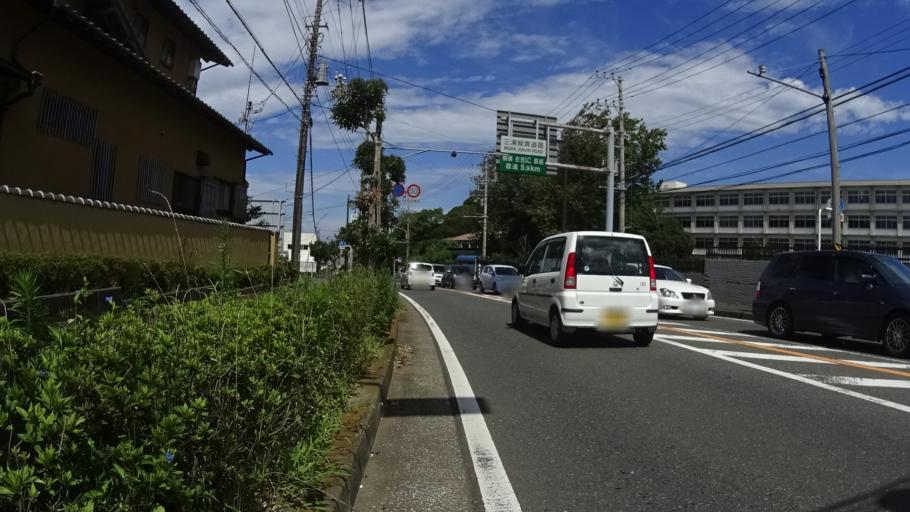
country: JP
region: Kanagawa
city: Miura
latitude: 35.1669
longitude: 139.6417
